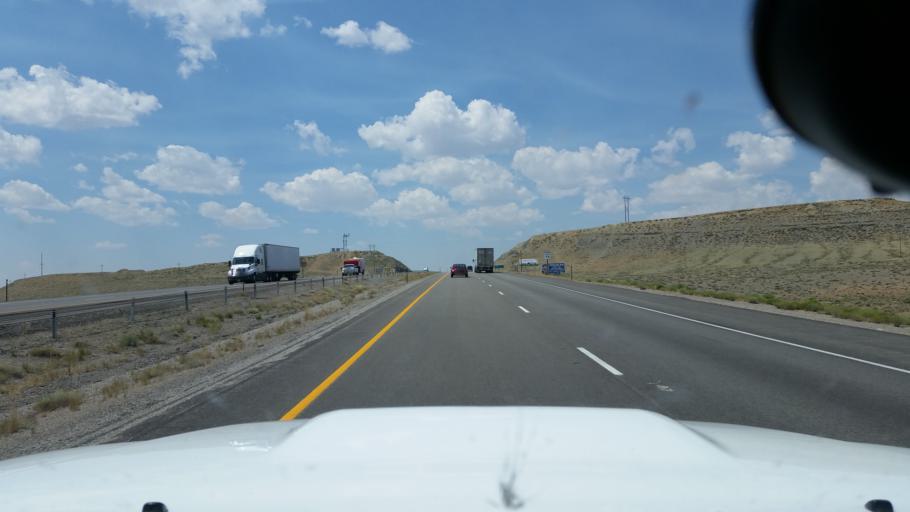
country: US
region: Wyoming
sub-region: Carbon County
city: Rawlins
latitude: 41.7819
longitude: -107.1359
